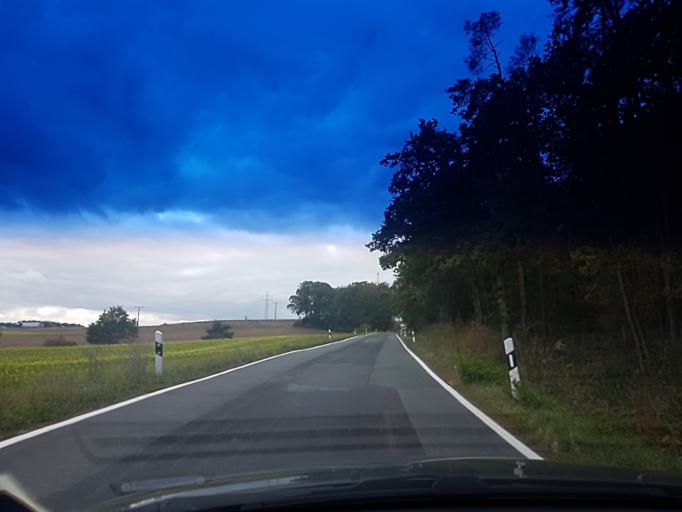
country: DE
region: Bavaria
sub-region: Regierungsbezirk Mittelfranken
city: Hochstadt an der Aisch
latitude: 49.7251
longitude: 10.8316
